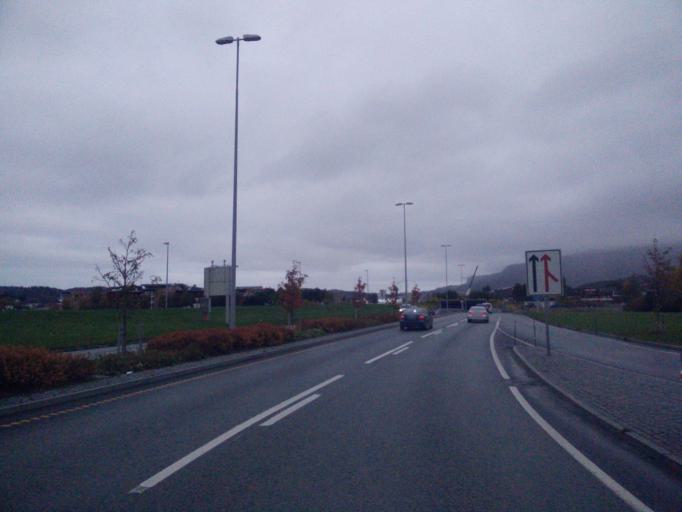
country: NO
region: Nord-Trondelag
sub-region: Stjordal
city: Stjordal
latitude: 63.4672
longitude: 10.9117
